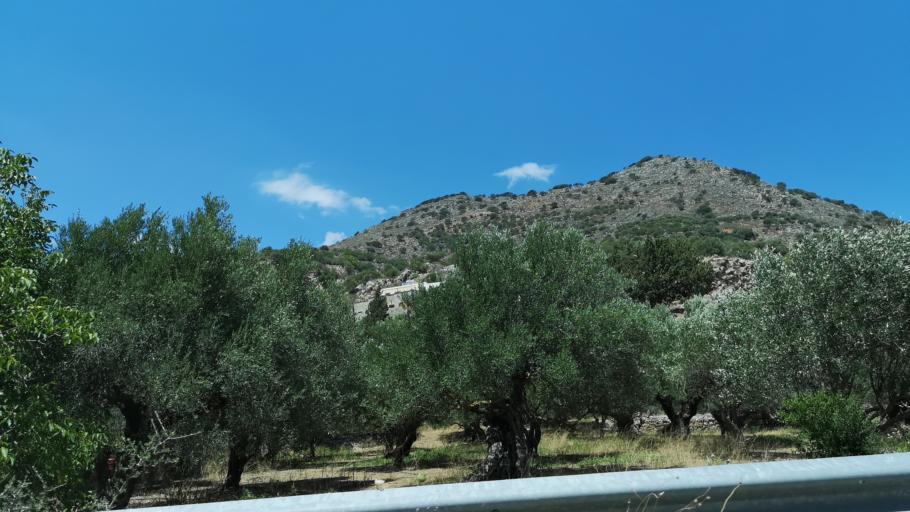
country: GR
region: Crete
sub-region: Nomos Lasithiou
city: Neapoli
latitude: 35.2488
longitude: 25.6244
